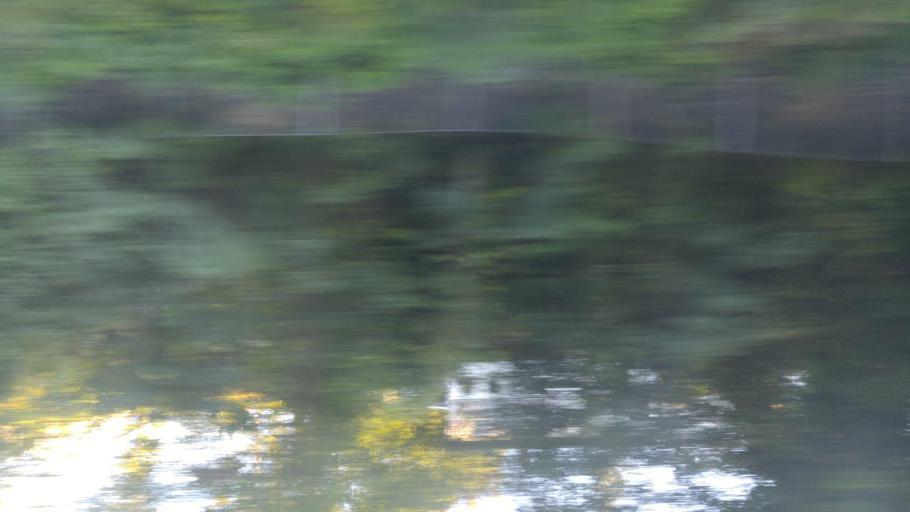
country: NO
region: Akershus
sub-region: Lorenskog
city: Kjenn
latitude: 59.9474
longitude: 10.9332
